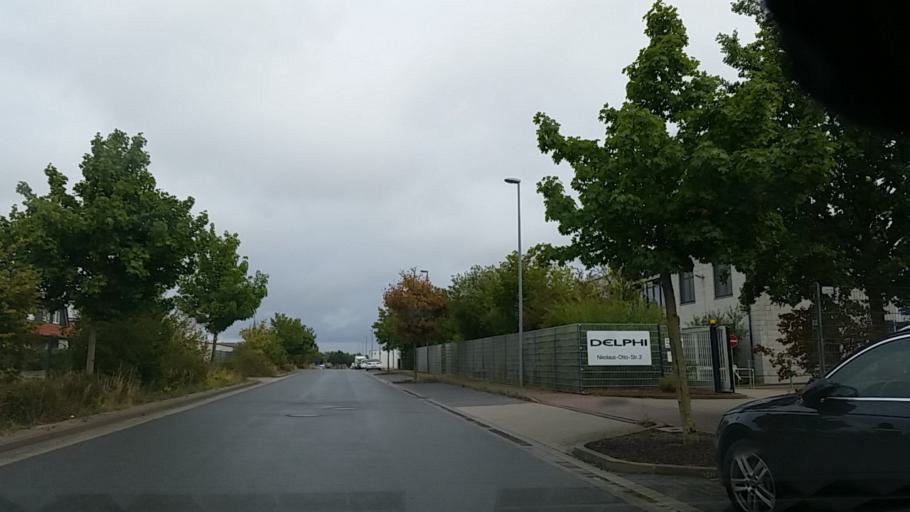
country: DE
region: Lower Saxony
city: Lehre
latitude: 52.3613
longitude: 10.7166
